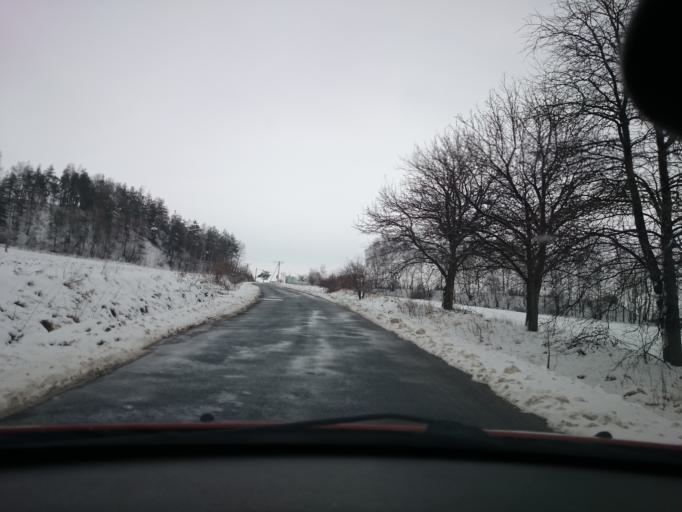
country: PL
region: Lower Silesian Voivodeship
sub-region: Powiat zabkowicki
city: Bardo
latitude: 50.5492
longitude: 16.7680
